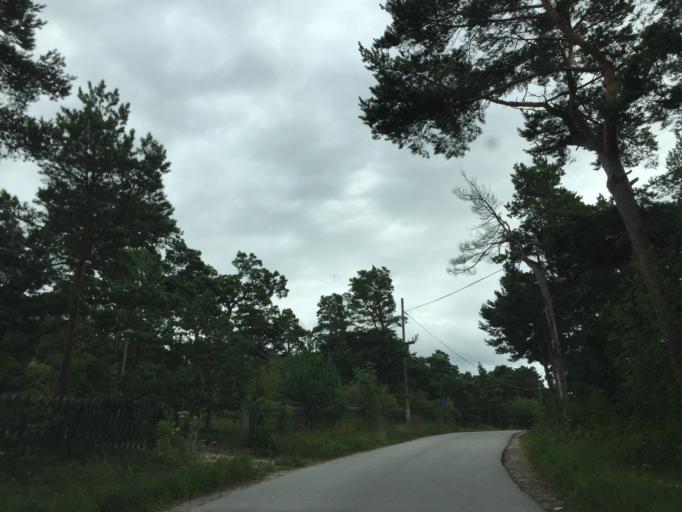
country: SE
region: Gotland
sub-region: Gotland
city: Visby
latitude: 57.7055
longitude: 18.3766
